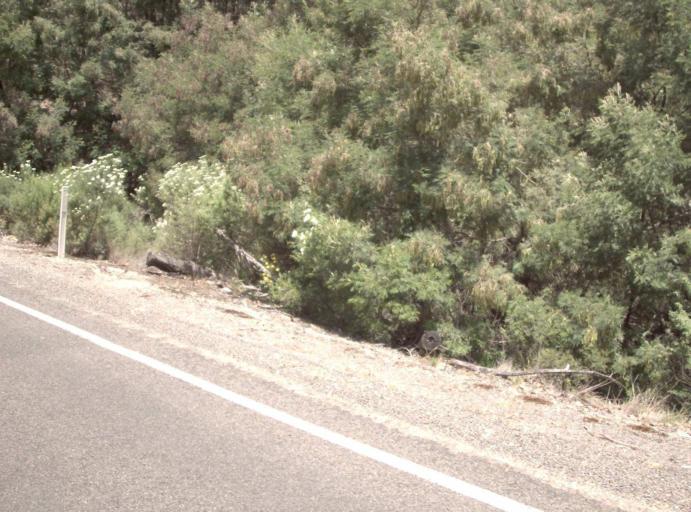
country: AU
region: Victoria
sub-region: East Gippsland
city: Lakes Entrance
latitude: -37.5702
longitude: 147.8901
